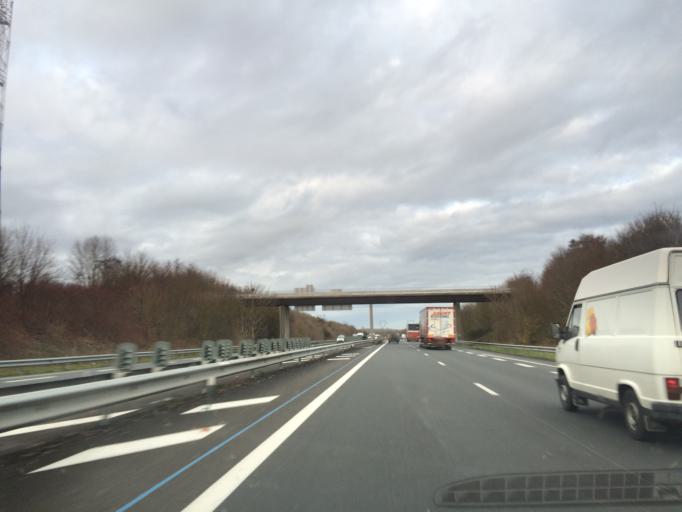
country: FR
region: Poitou-Charentes
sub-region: Departement des Deux-Sevres
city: Fors
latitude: 46.2404
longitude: -0.4340
